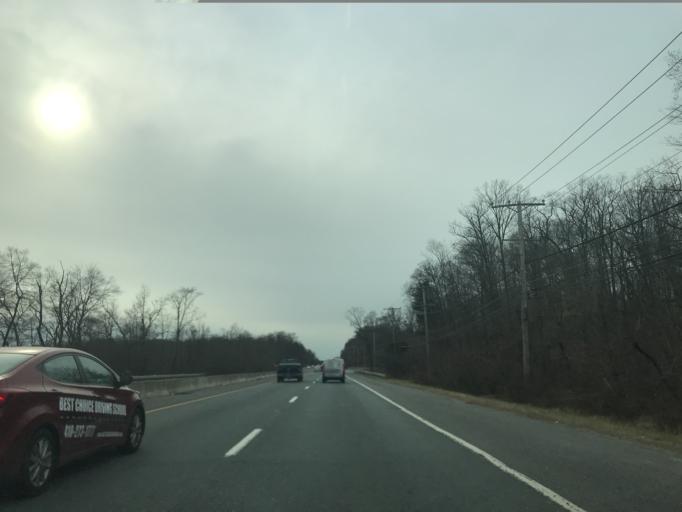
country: US
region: Maryland
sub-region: Harford County
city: Perryman
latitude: 39.4796
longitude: -76.2177
